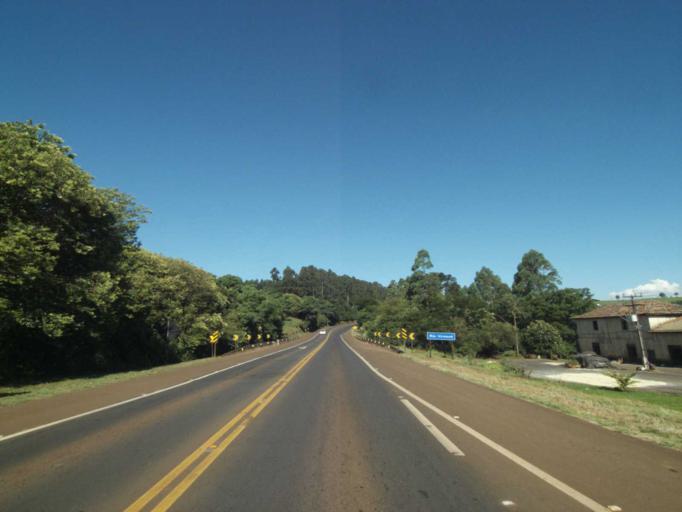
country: BR
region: Parana
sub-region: Laranjeiras Do Sul
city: Laranjeiras do Sul
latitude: -25.3783
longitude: -52.2013
